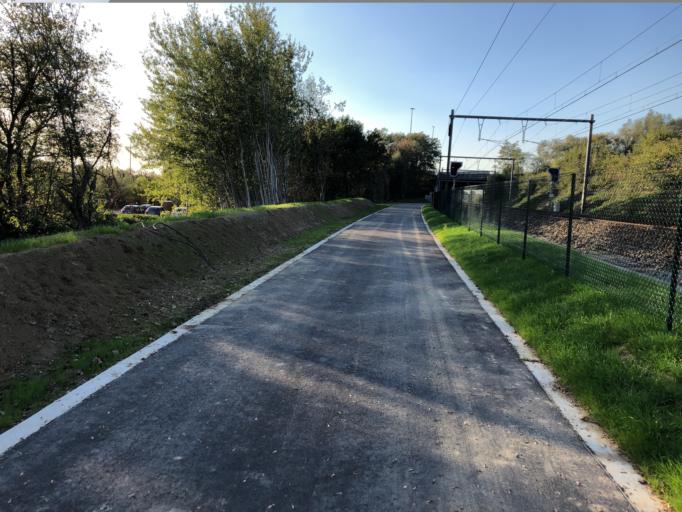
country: BE
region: Flanders
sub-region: Provincie Vlaams-Brabant
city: Wemmel
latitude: 50.8829
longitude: 4.2893
